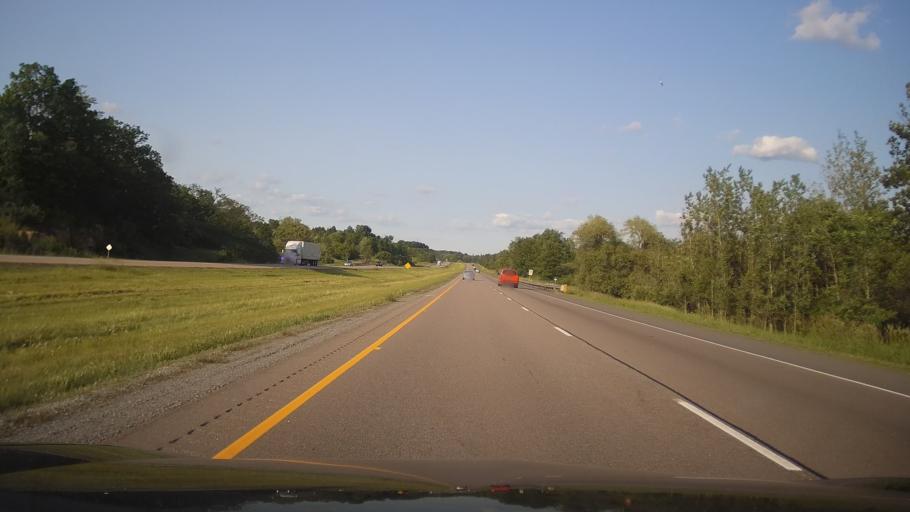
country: CA
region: Ontario
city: Gananoque
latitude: 44.3463
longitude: -76.1219
